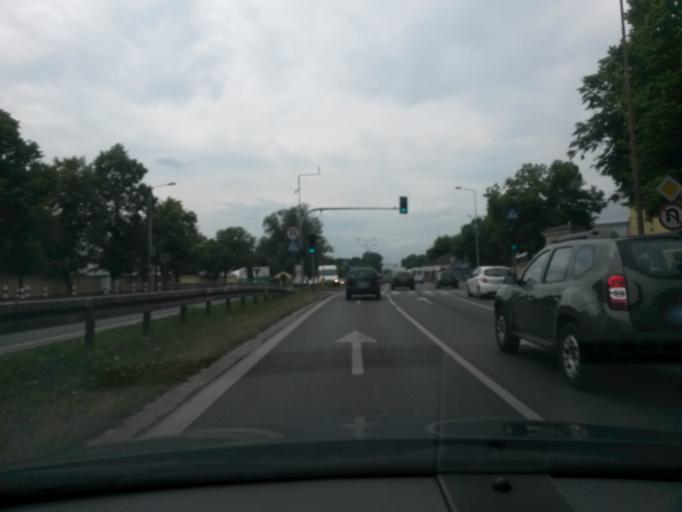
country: PL
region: Masovian Voivodeship
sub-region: Powiat pruszkowski
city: Raszyn
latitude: 52.1506
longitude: 20.9167
